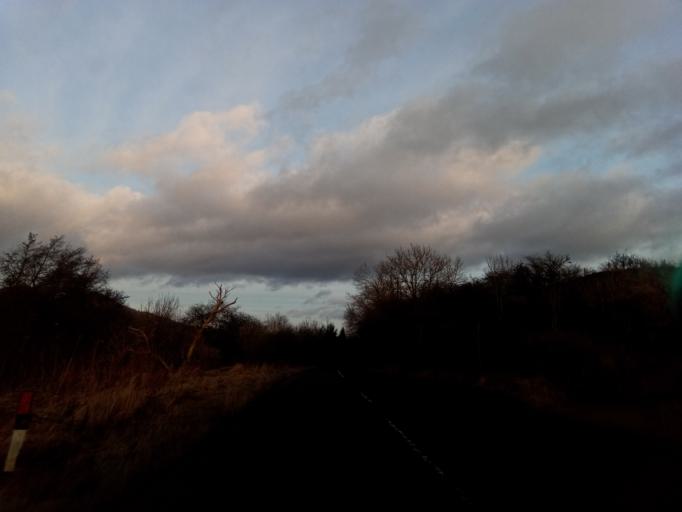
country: GB
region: Scotland
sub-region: The Scottish Borders
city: Melrose
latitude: 55.5542
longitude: -2.7367
